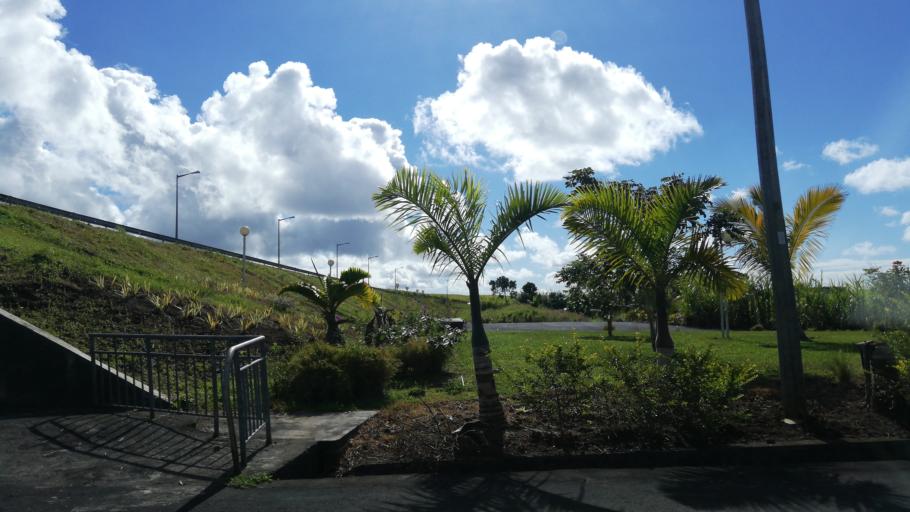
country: MU
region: Moka
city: Quartier Militaire
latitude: -20.2433
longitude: 57.5935
